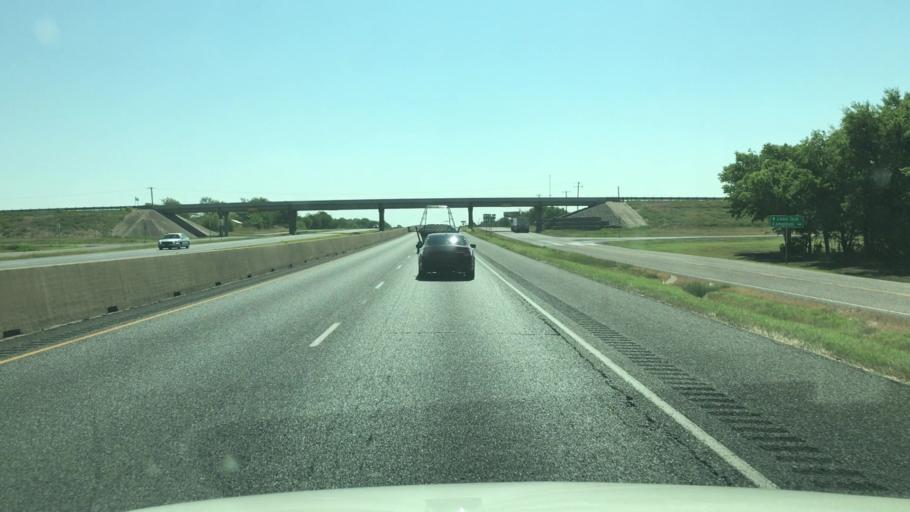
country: US
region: Texas
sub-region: Hunt County
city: Commerce
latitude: 33.1319
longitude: -95.9492
